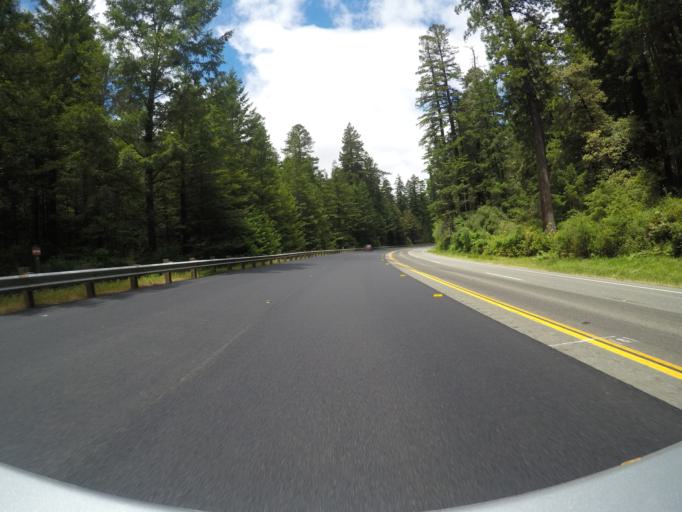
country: US
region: California
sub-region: Humboldt County
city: Redway
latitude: 40.2884
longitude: -123.8961
